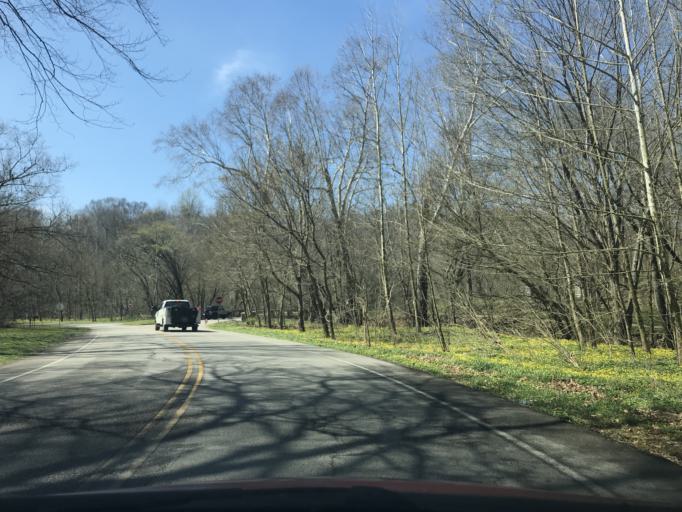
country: US
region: Kentucky
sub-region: Jefferson County
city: Saint Matthews
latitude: 38.2396
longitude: -85.6929
